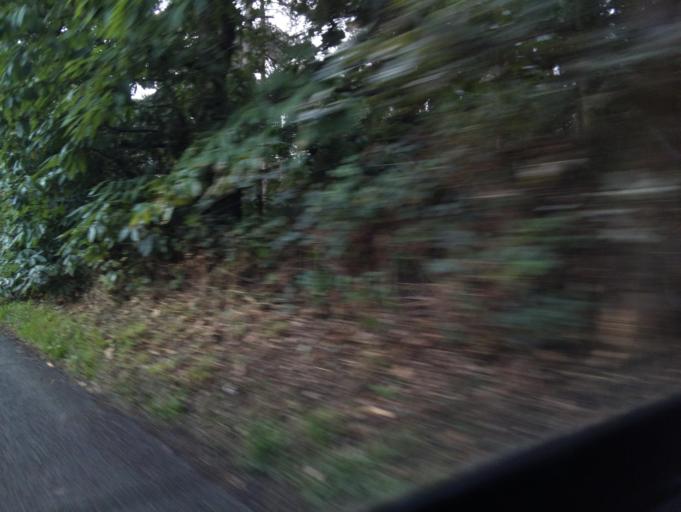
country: GB
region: England
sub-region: Staffordshire
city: Barlaston
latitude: 52.9275
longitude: -2.2022
